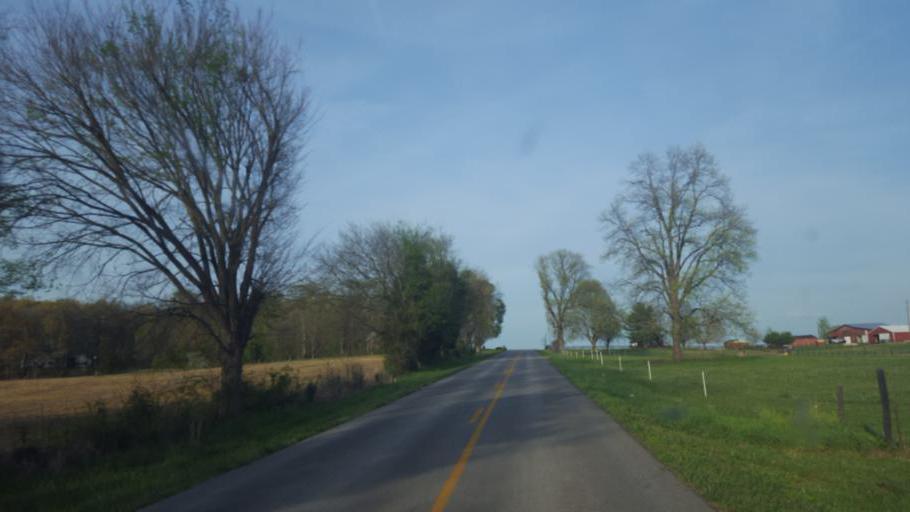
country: US
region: Kentucky
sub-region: Barren County
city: Glasgow
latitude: 36.9403
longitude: -86.0616
